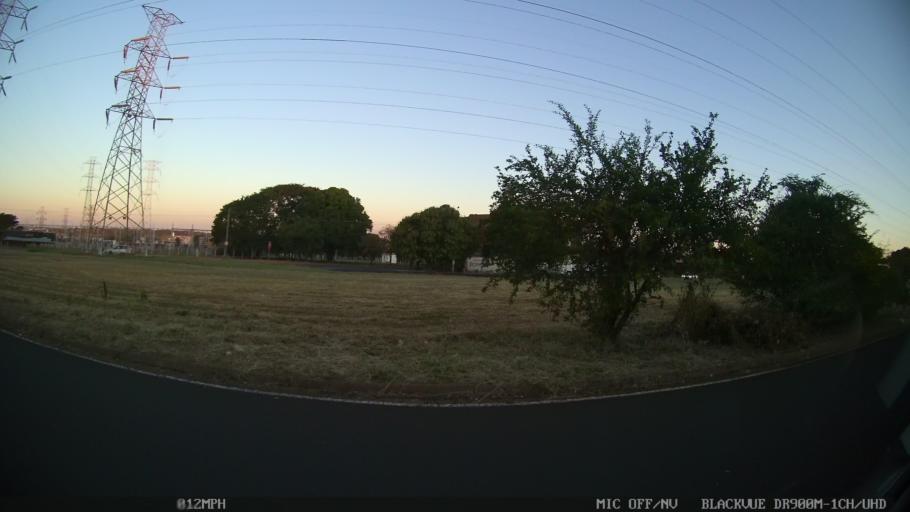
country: BR
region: Sao Paulo
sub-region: Sao Jose Do Rio Preto
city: Sao Jose do Rio Preto
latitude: -20.8426
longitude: -49.3755
